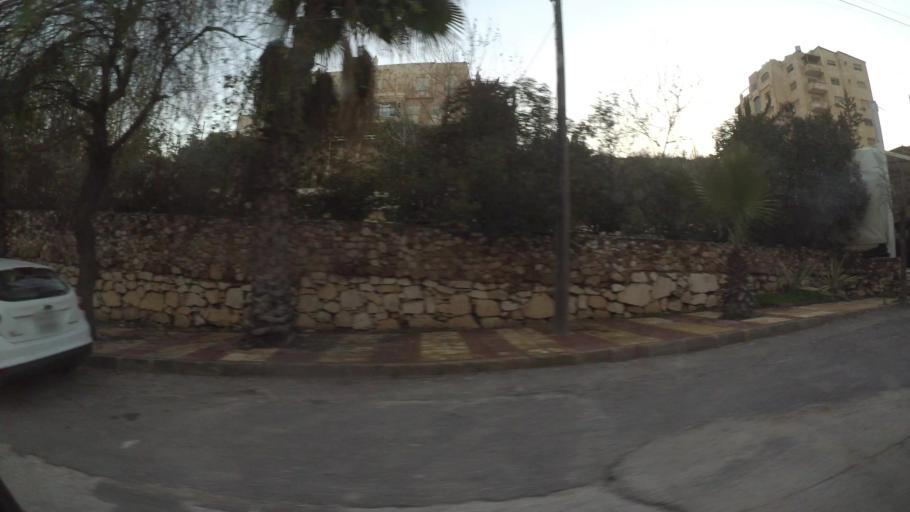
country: JO
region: Amman
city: Al Jubayhah
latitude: 32.0026
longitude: 35.8536
